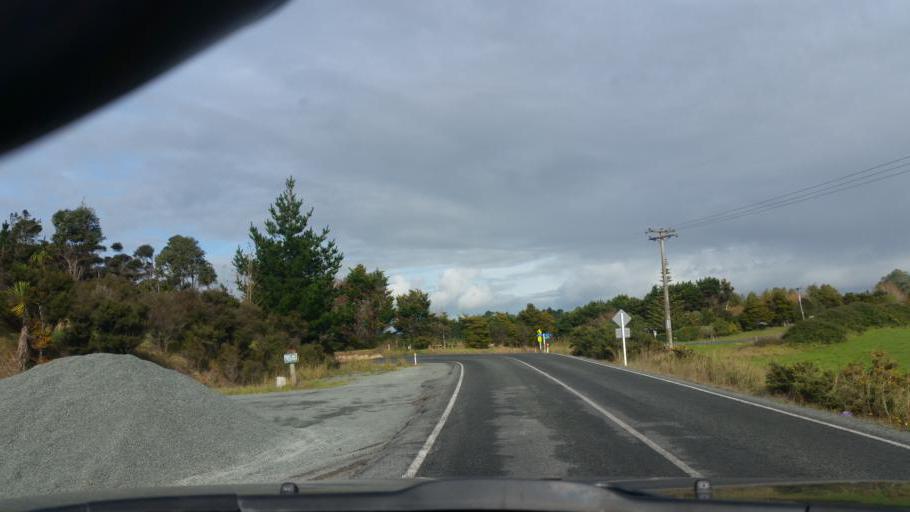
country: NZ
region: Auckland
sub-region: Auckland
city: Wellsford
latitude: -36.1134
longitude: 174.5406
